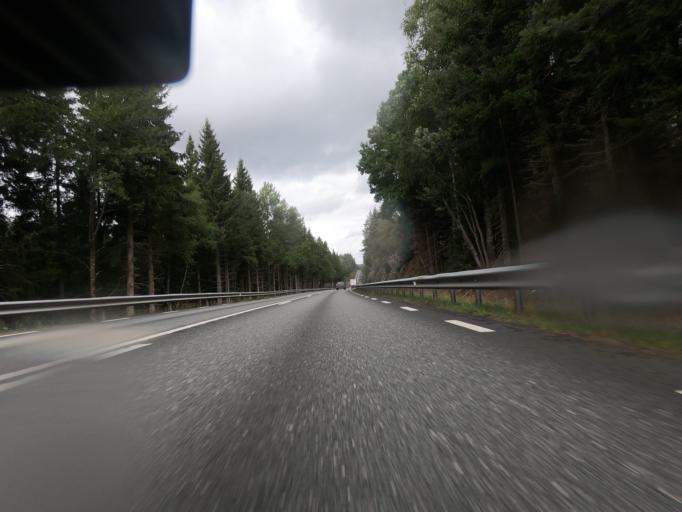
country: SE
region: Joenkoeping
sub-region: Savsjo Kommun
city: Vrigstad
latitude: 57.4259
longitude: 14.3246
